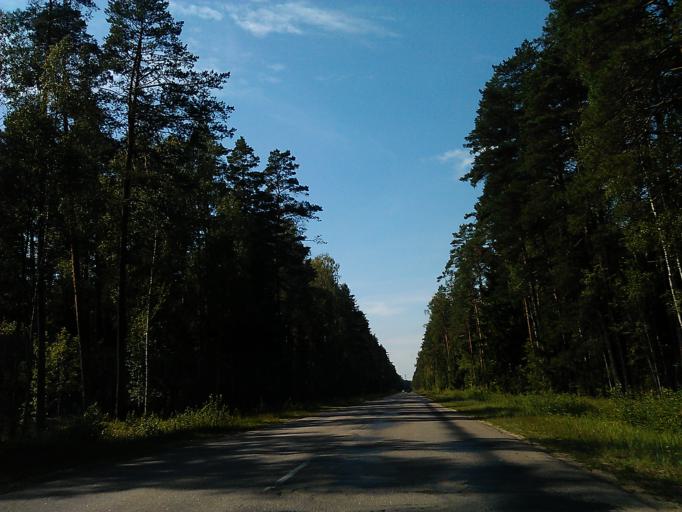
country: LV
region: Garkalne
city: Garkalne
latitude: 56.9436
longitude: 24.4319
